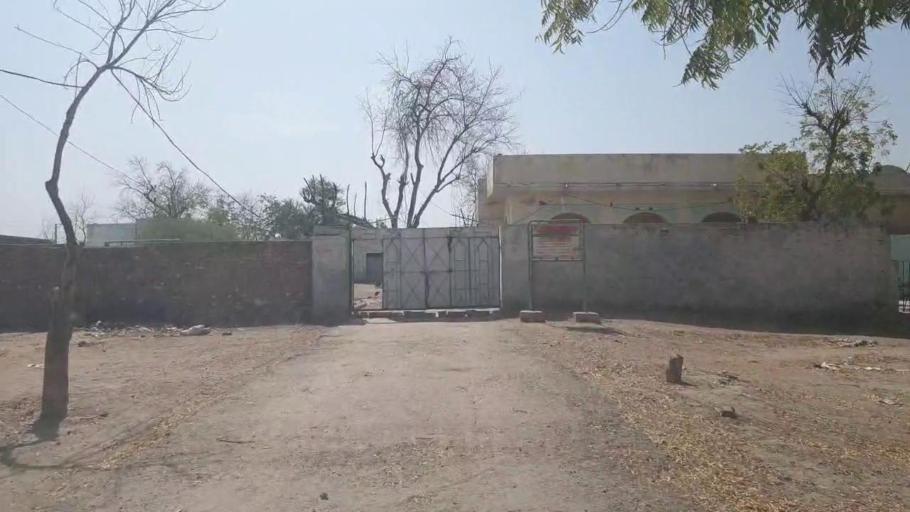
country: PK
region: Sindh
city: Kunri
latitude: 25.2512
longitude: 69.5939
